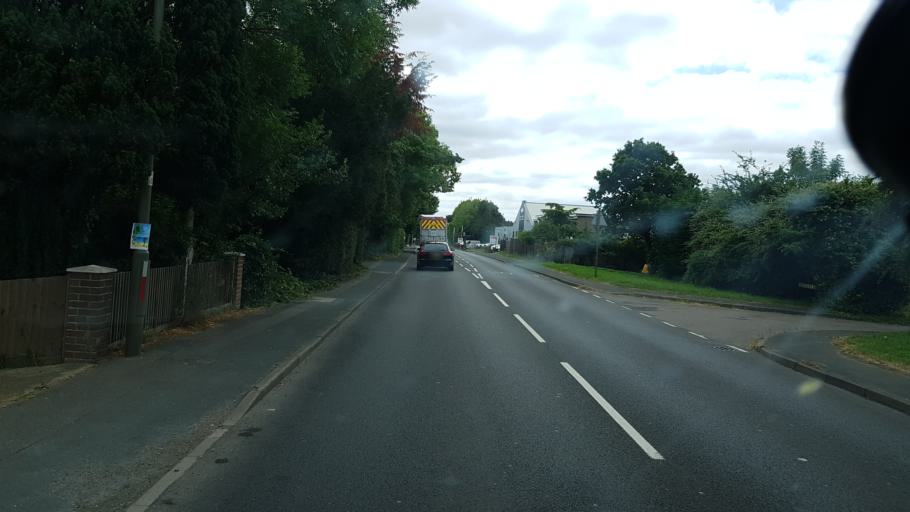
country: GB
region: England
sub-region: Surrey
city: Lingfield
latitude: 51.1955
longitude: -0.0524
